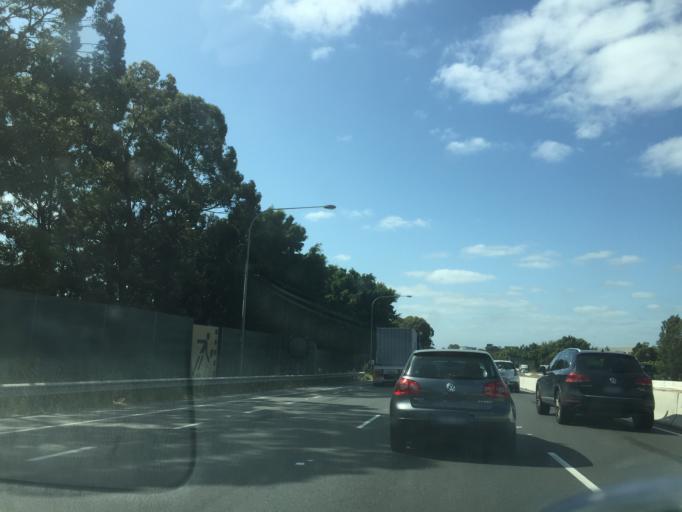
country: AU
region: New South Wales
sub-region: Auburn
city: Auburn
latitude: -33.8454
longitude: 151.0484
